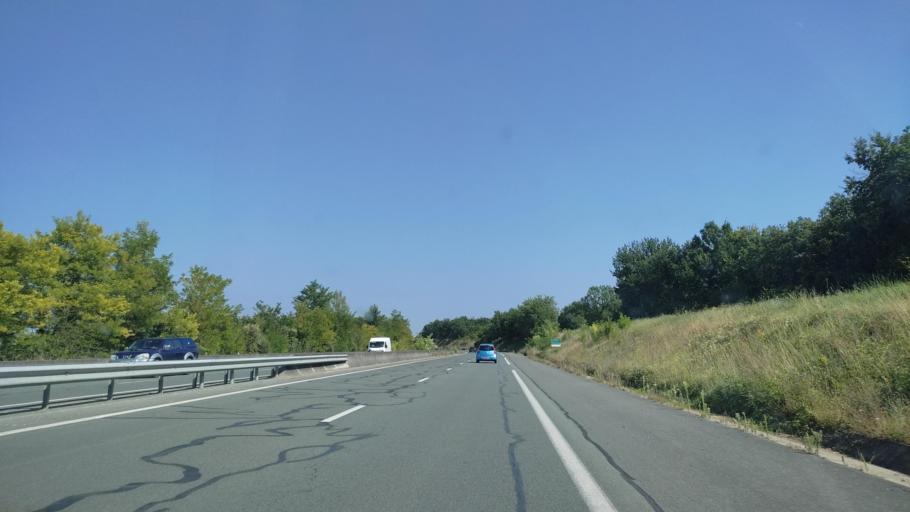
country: FR
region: Poitou-Charentes
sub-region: Departement de la Charente
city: Saint-Yrieix-sur-Charente
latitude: 45.6818
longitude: 0.1212
